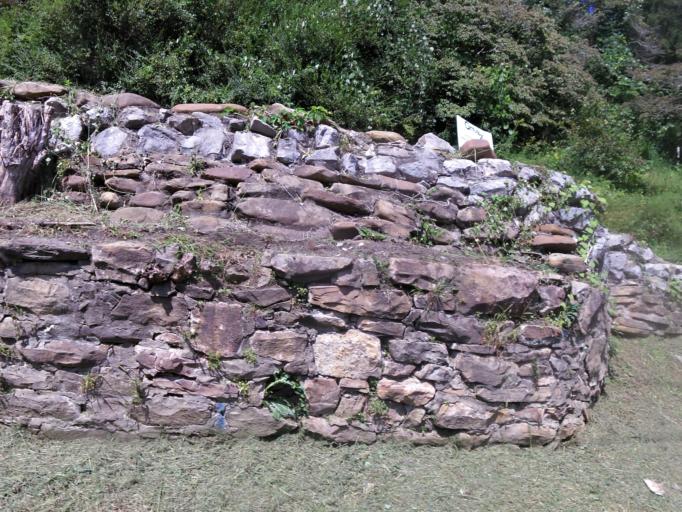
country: US
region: Kentucky
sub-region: Harlan County
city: Harlan
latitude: 36.8482
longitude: -83.3175
